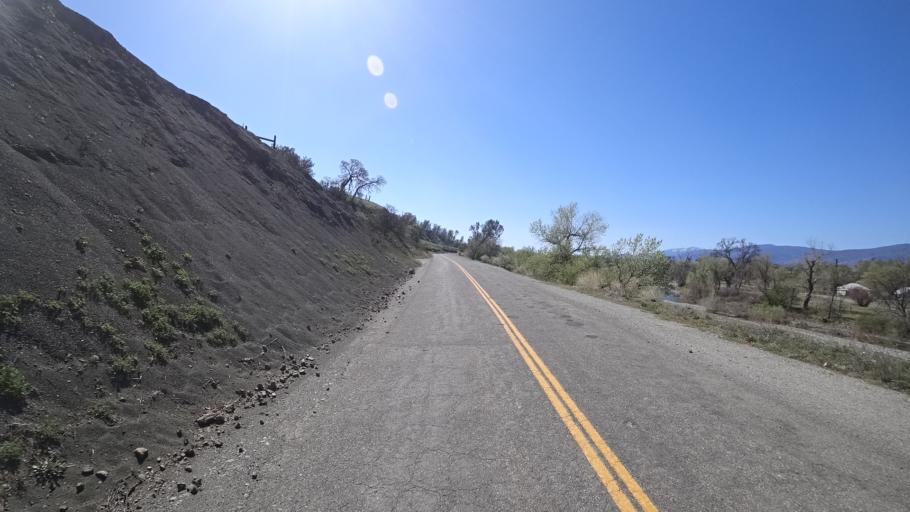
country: US
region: California
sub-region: Glenn County
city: Orland
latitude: 39.6766
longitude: -122.5242
